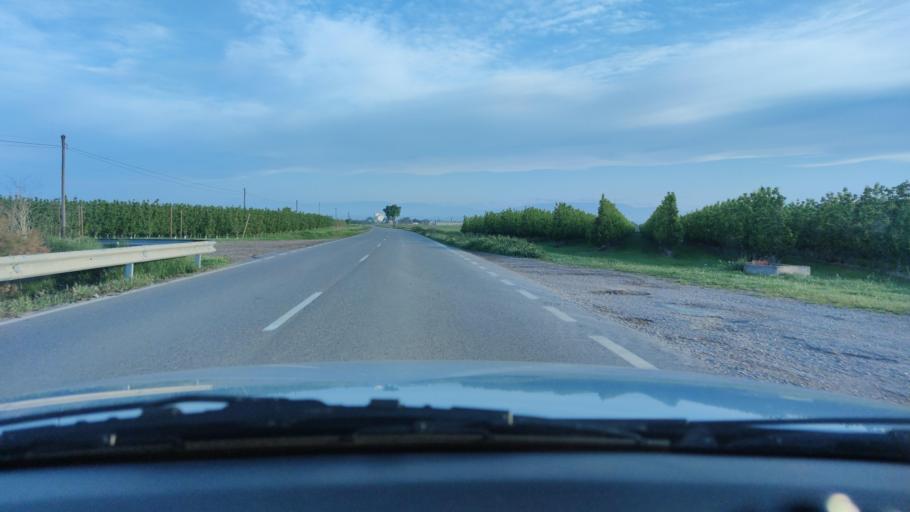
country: ES
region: Catalonia
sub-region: Provincia de Lleida
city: Ivars d'Urgell
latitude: 41.6634
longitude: 0.9937
